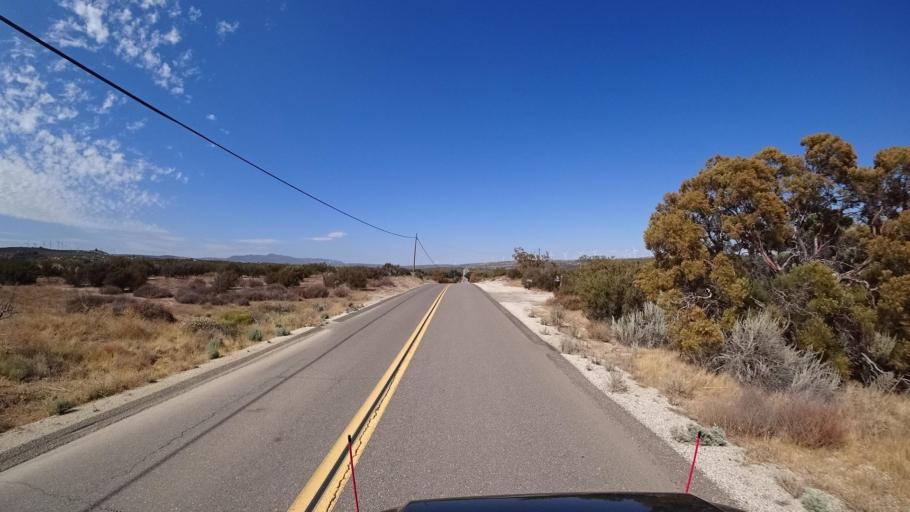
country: US
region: California
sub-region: San Diego County
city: Campo
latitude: 32.6852
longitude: -116.2937
